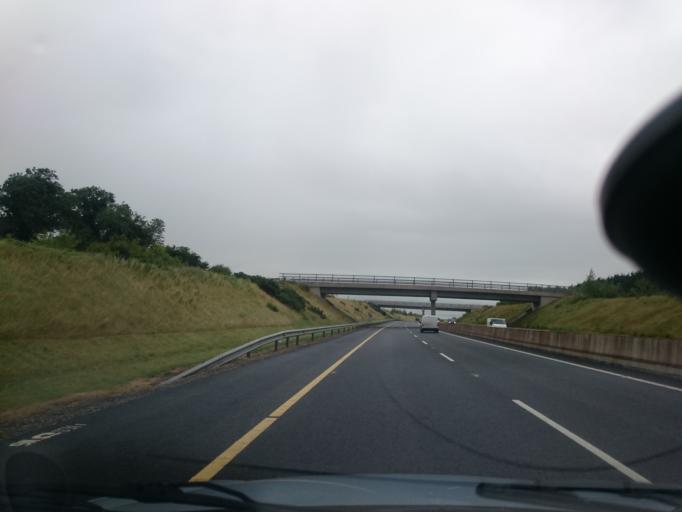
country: IE
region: Leinster
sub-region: Kildare
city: Castledermot
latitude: 52.9252
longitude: -6.8667
